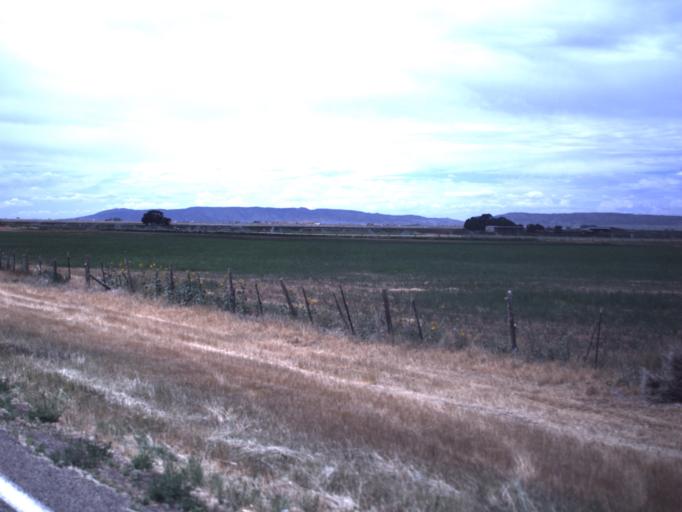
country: US
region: Utah
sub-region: Iron County
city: Parowan
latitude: 37.8775
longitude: -112.7830
